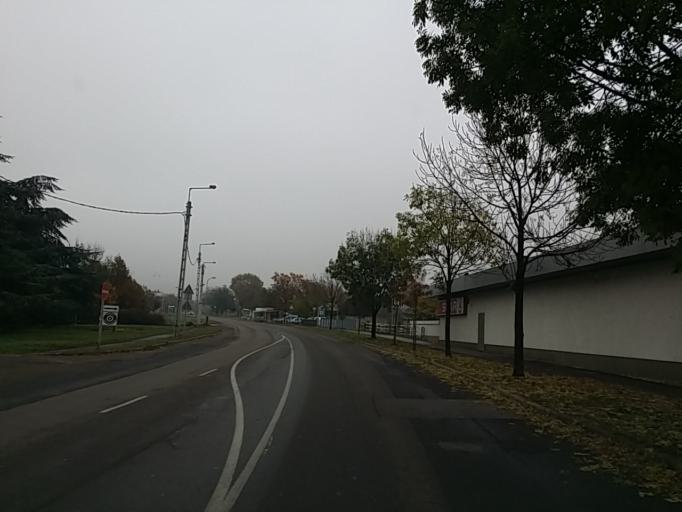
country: HU
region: Heves
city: Gyongyos
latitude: 47.7891
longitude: 19.9367
